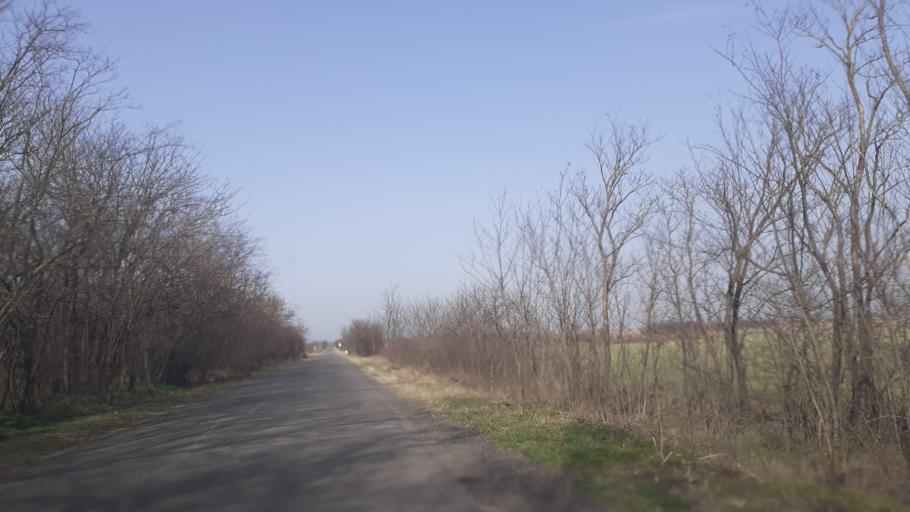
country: HU
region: Pest
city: Dabas
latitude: 47.1246
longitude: 19.2102
